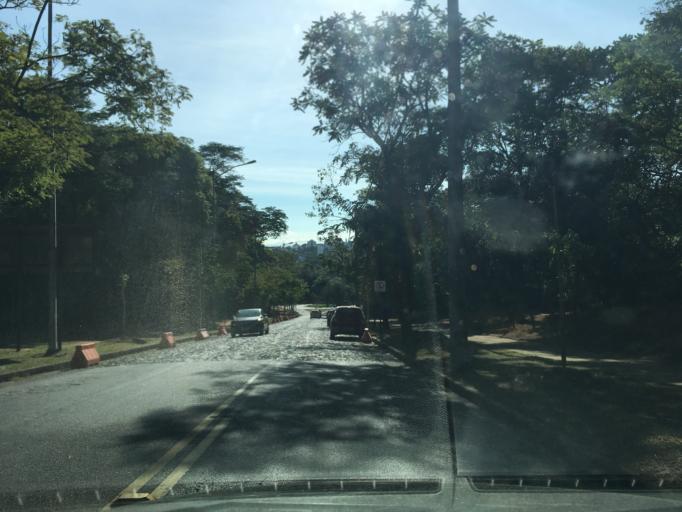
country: BR
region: Minas Gerais
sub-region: Belo Horizonte
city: Belo Horizonte
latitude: -19.8632
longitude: -43.9661
